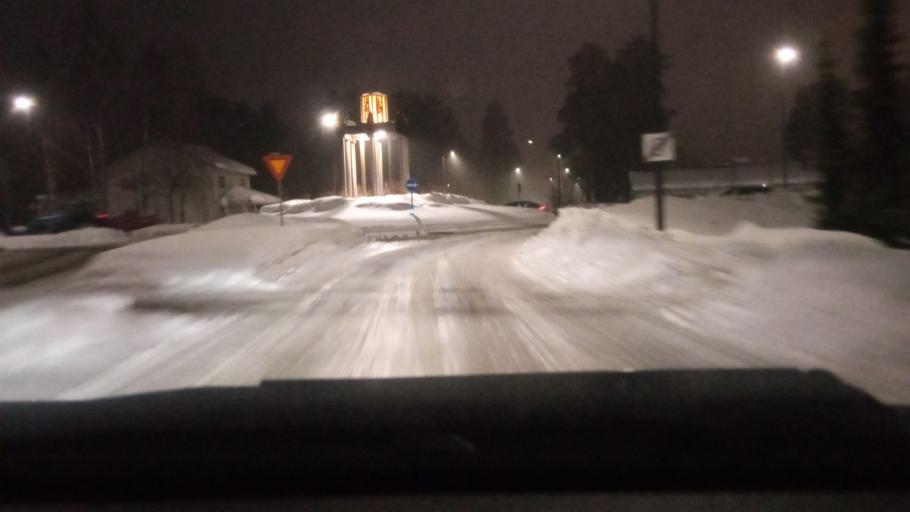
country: FI
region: Southern Ostrobothnia
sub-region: Jaerviseutu
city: Alajaervi
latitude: 62.9992
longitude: 23.8111
